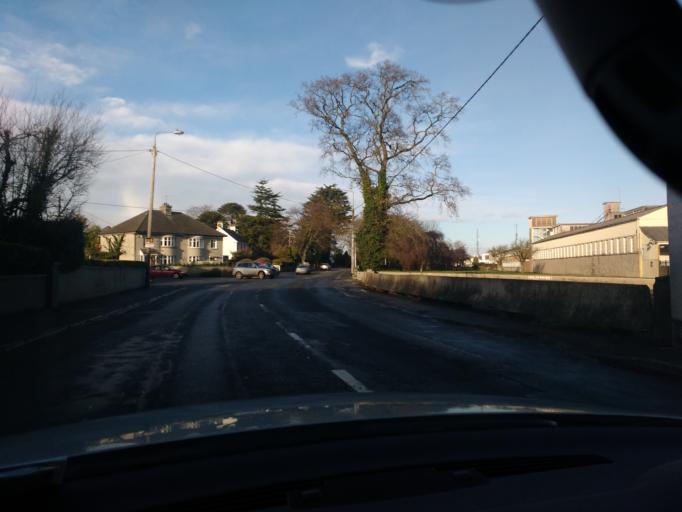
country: IE
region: Munster
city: Thurles
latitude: 52.6724
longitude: -7.8122
